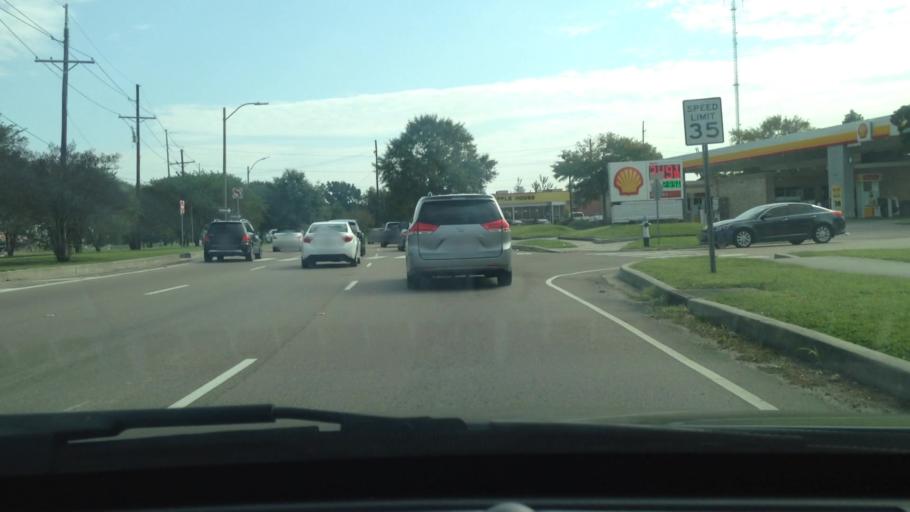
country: US
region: Louisiana
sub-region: Jefferson Parish
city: Terrytown
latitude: 29.9292
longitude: -90.0324
